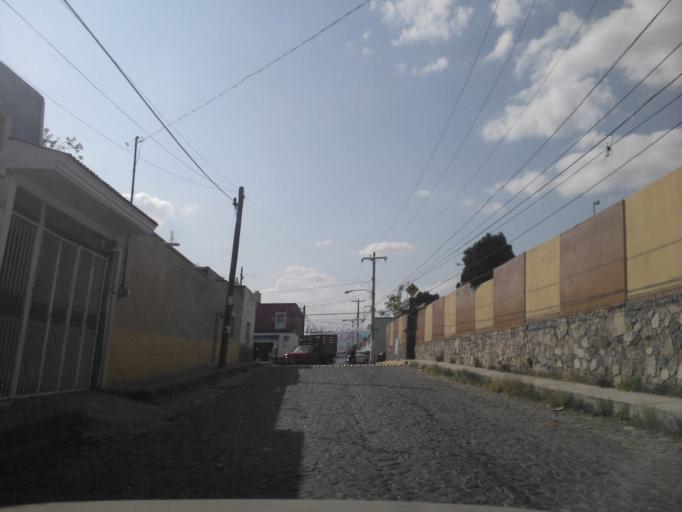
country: MX
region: Jalisco
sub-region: San Pedro Tlaquepaque
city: Paseo del Prado
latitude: 20.5886
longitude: -103.3868
